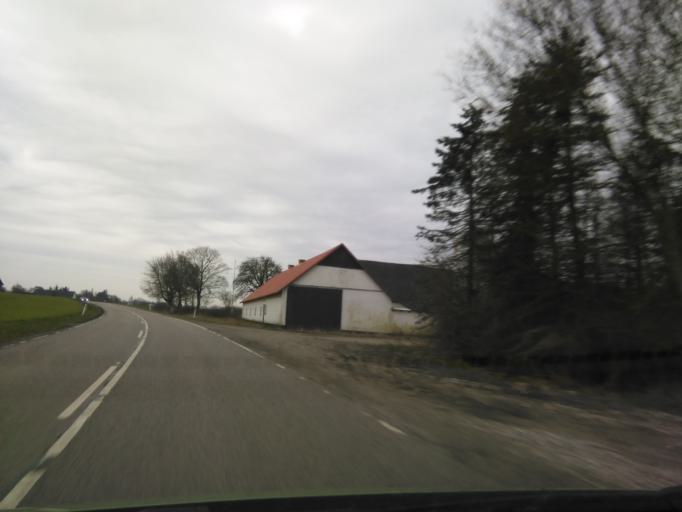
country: DK
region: Central Jutland
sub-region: Randers Kommune
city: Spentrup
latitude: 56.5829
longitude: 9.9938
